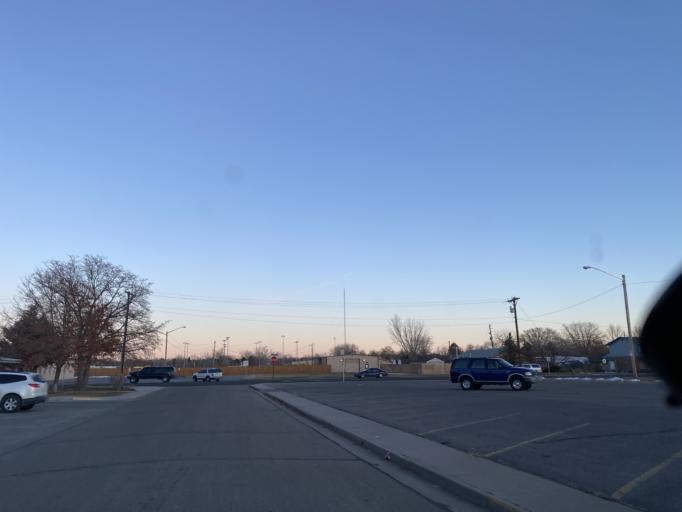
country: US
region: Colorado
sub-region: Adams County
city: Brighton
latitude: 39.9766
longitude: -104.8134
